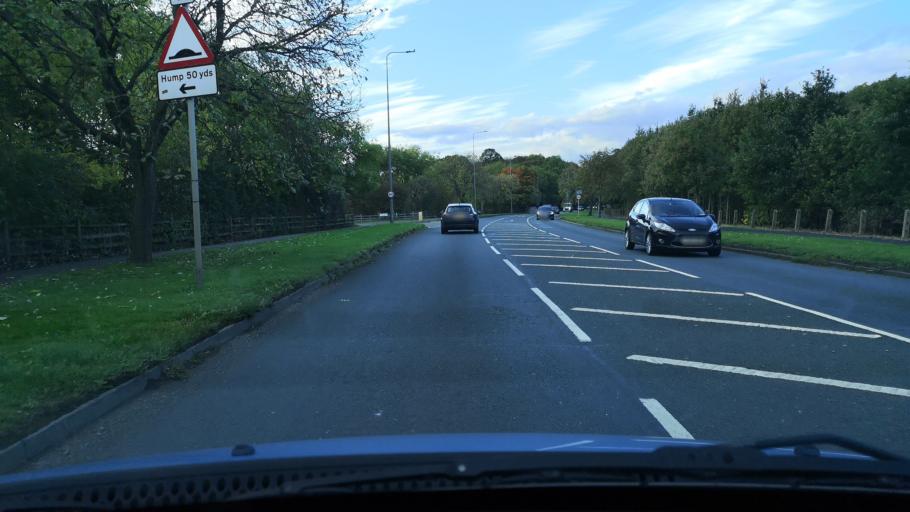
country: GB
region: England
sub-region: North Lincolnshire
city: Scunthorpe
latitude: 53.5804
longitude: -0.6682
